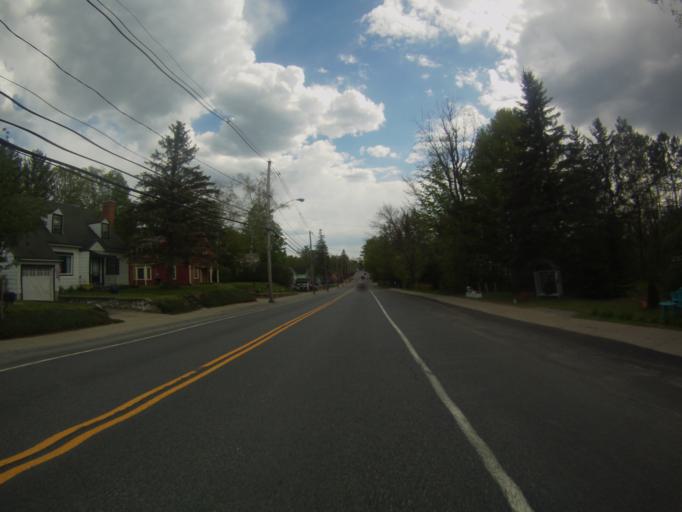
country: US
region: New York
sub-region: Essex County
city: Ticonderoga
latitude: 43.8431
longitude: -73.7596
